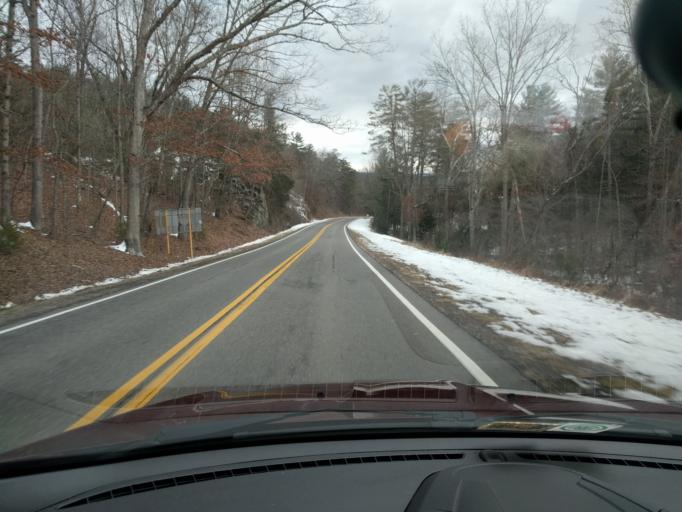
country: US
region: Virginia
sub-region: Alleghany County
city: Clifton Forge
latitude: 37.8269
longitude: -79.7579
